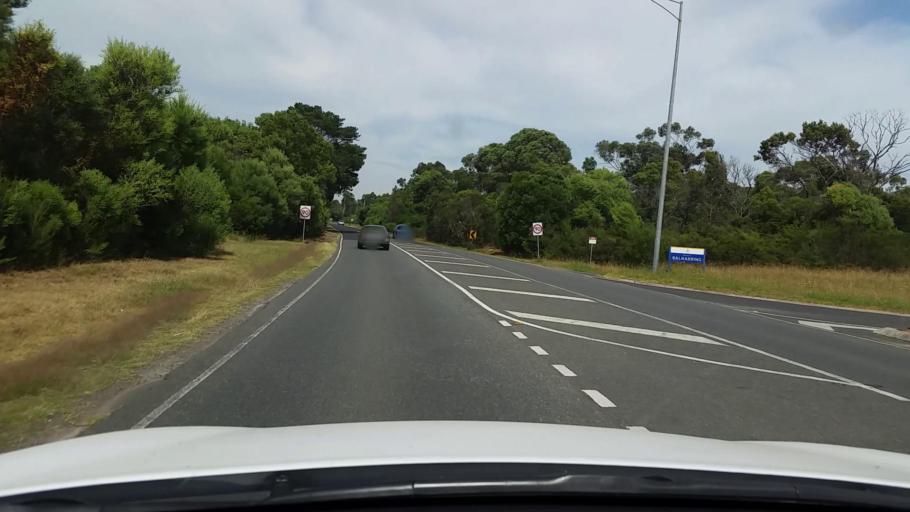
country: AU
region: Victoria
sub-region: Mornington Peninsula
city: Balnarring
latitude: -38.3540
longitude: 145.1546
